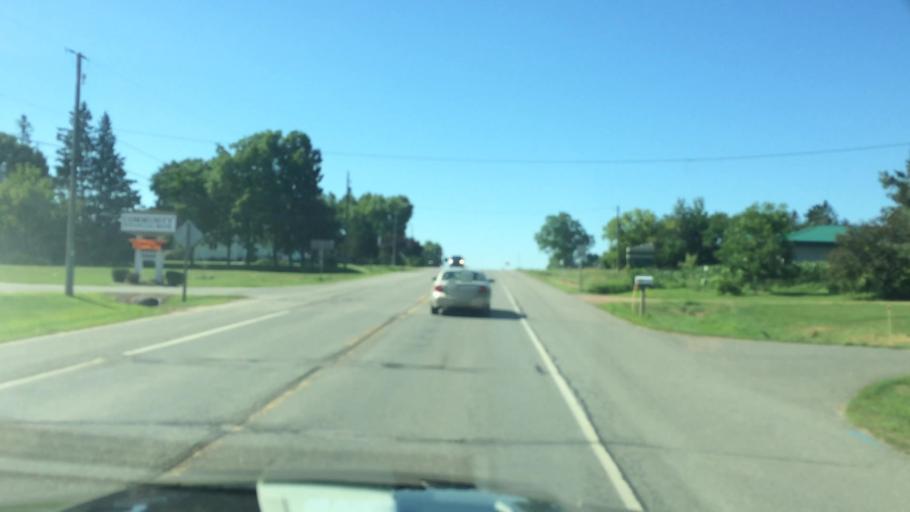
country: US
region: Wisconsin
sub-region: Marathon County
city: Stratford
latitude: 44.7934
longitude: -90.0792
